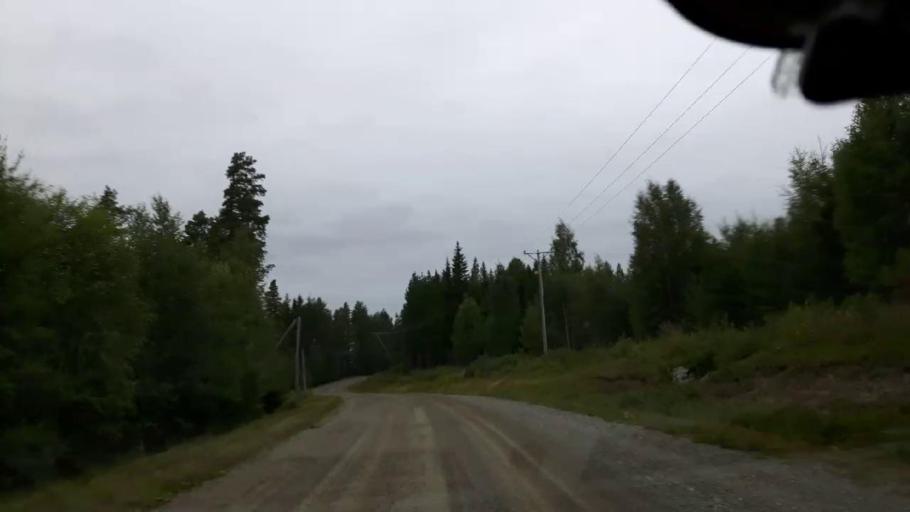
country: SE
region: Vaesternorrland
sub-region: Ange Kommun
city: Fransta
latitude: 62.7940
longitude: 16.0354
